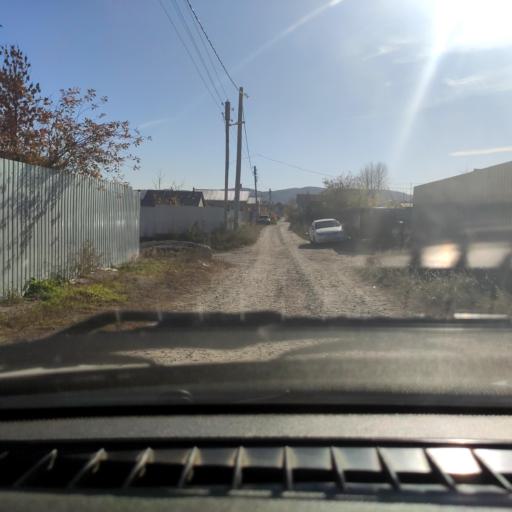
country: RU
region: Samara
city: Zhigulevsk
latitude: 53.4670
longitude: 49.5871
